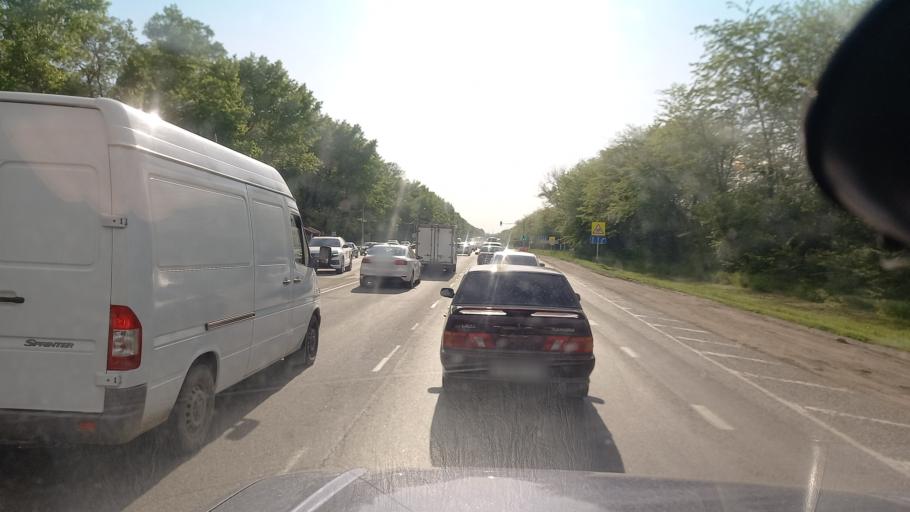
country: RU
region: Adygeya
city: Yablonovskiy
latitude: 45.0566
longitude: 38.8873
